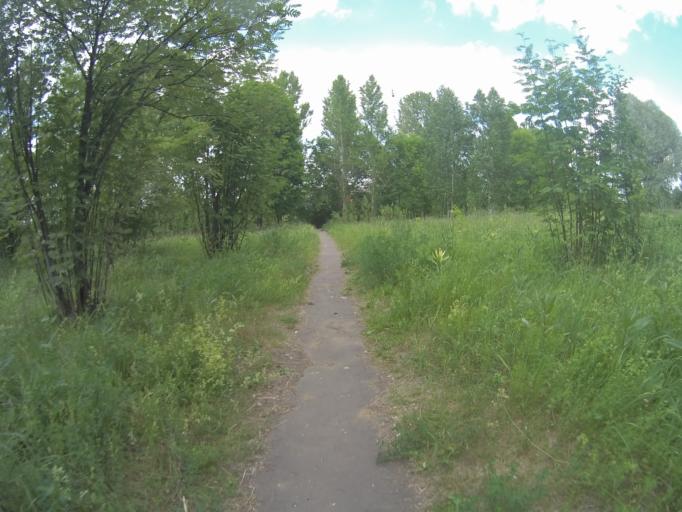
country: RU
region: Vladimir
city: Suzdal'
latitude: 56.4421
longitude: 40.4579
